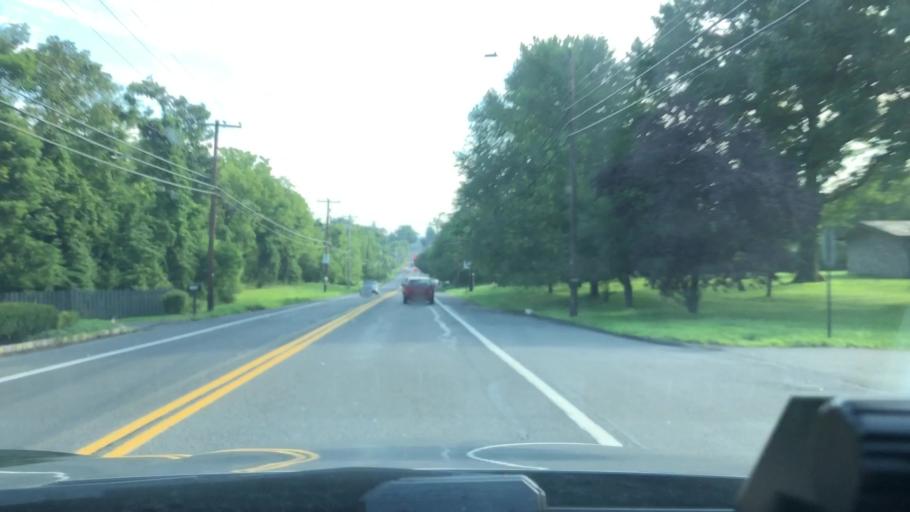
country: US
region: Pennsylvania
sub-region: Northampton County
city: Middletown
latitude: 40.6647
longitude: -75.3509
